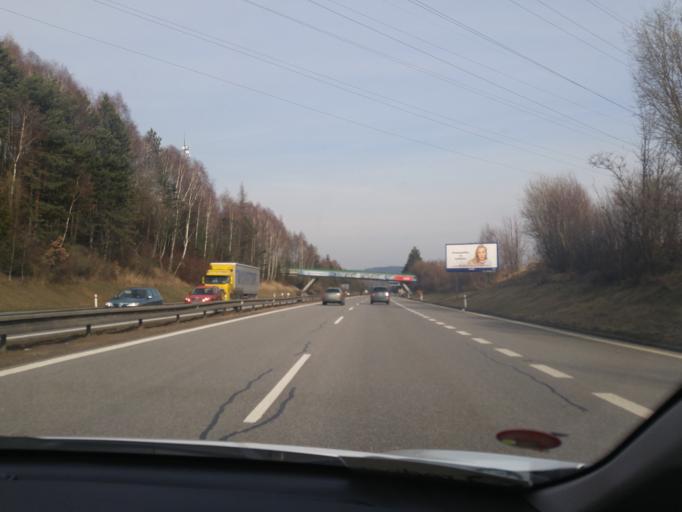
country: CZ
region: Vysocina
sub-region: Okres Pelhrimov
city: Humpolec
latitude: 49.5396
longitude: 15.3319
